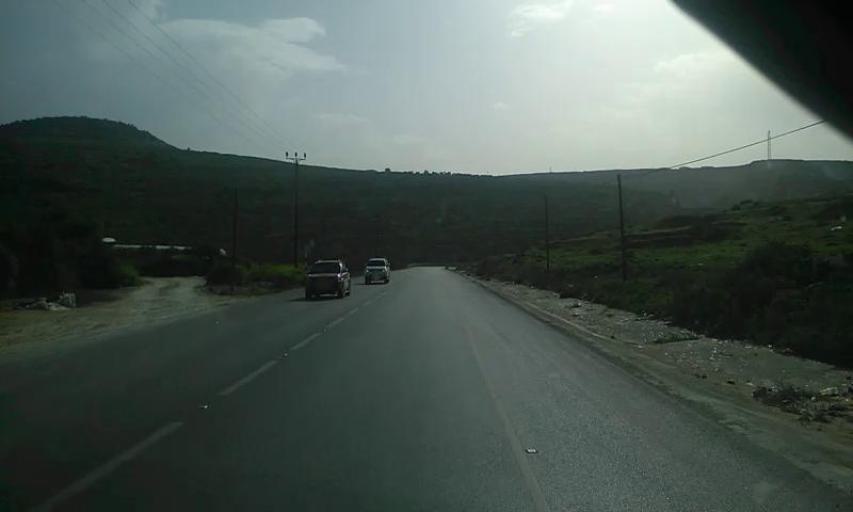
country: PS
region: West Bank
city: Dayr Sharaf
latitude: 32.2540
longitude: 35.1802
